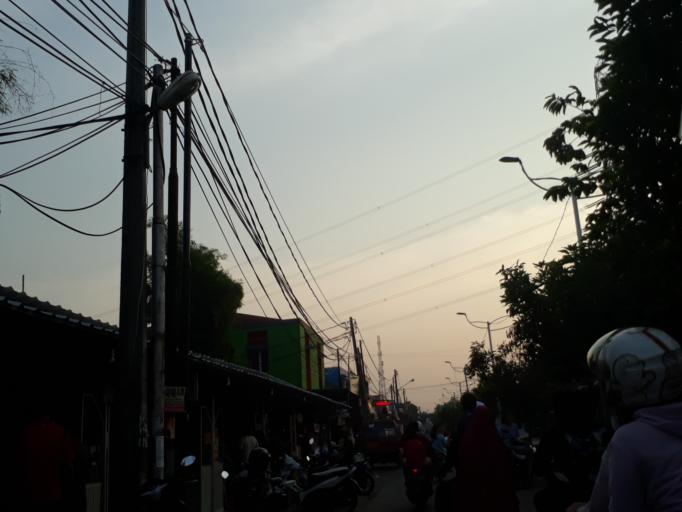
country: ID
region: West Java
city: Bekasi
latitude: -6.2433
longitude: 107.0493
